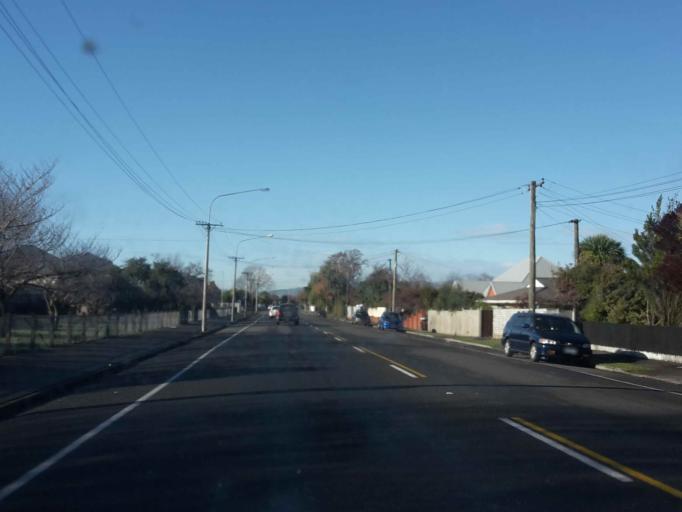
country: NZ
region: Canterbury
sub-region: Christchurch City
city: Christchurch
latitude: -43.4999
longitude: 172.5869
